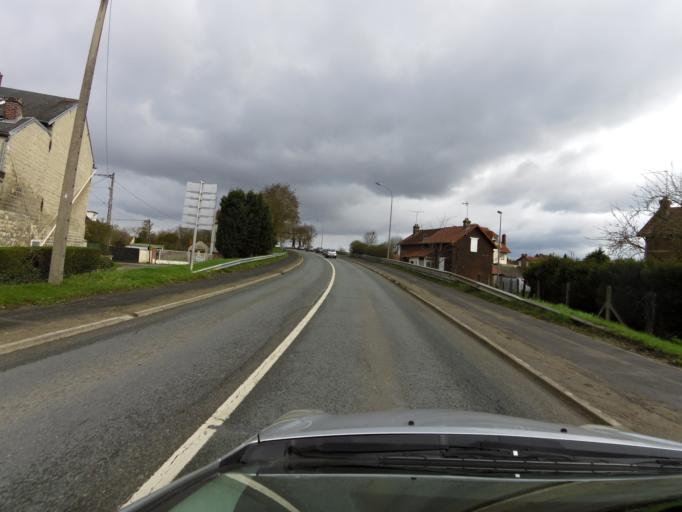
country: FR
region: Picardie
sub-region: Departement de l'Oise
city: Pont-Sainte-Maxence
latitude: 49.3090
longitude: 2.6056
